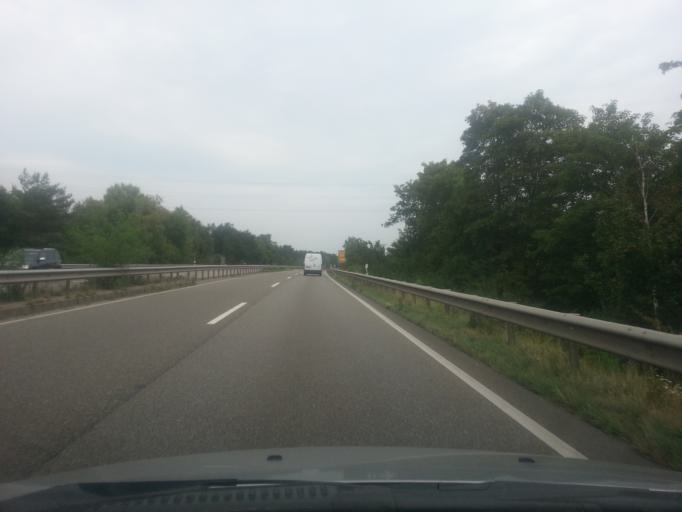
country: DE
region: Rheinland-Pfalz
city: Speyer
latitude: 49.3388
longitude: 8.4110
